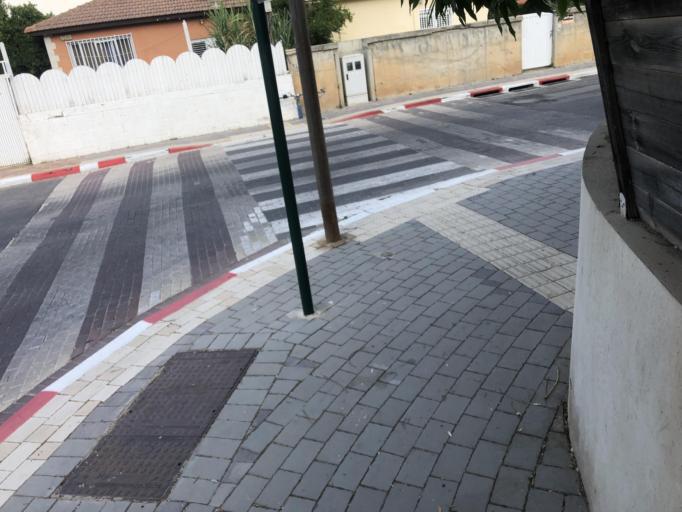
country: IL
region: Central District
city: Yehud
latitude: 32.0326
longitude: 34.8832
